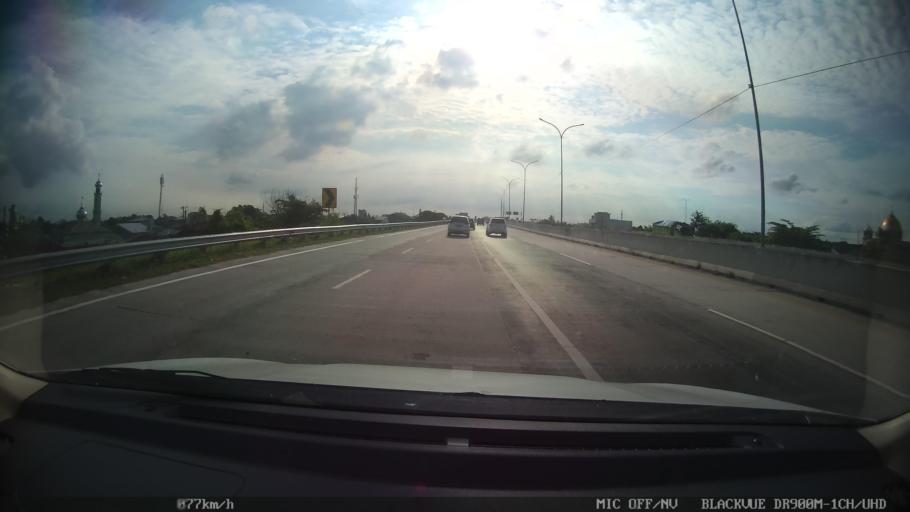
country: ID
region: North Sumatra
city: Medan
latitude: 3.6475
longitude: 98.6737
